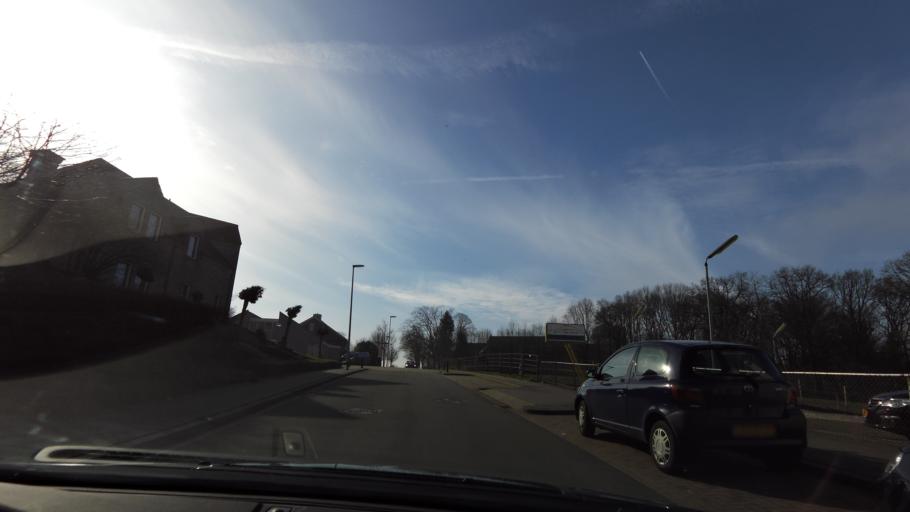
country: NL
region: Limburg
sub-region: Gemeente Heerlen
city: Heerlen
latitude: 50.8684
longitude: 5.9924
